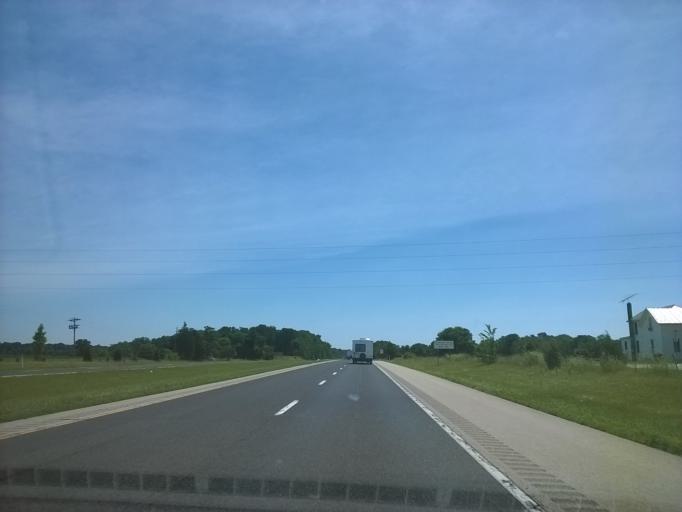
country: US
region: Indiana
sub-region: Ripley County
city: Batesville
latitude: 39.3167
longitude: -85.3074
